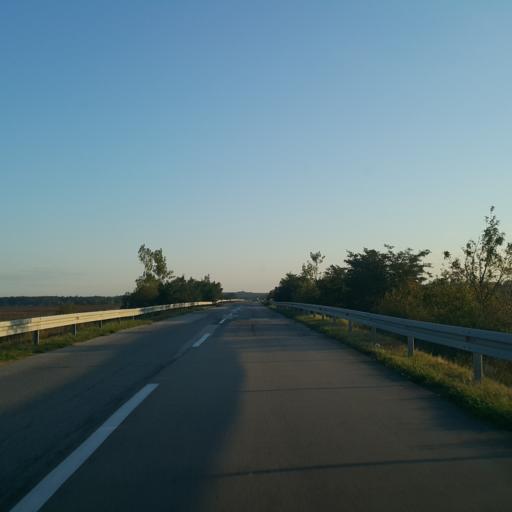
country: RS
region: Central Serbia
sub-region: Borski Okrug
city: Negotin
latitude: 44.1362
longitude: 22.3470
